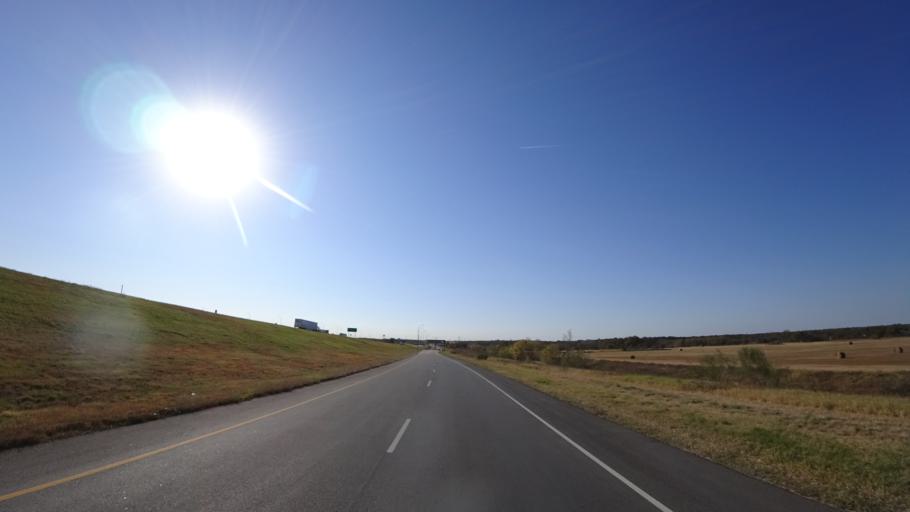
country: US
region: Texas
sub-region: Williamson County
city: Hutto
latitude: 30.5346
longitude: -97.5770
